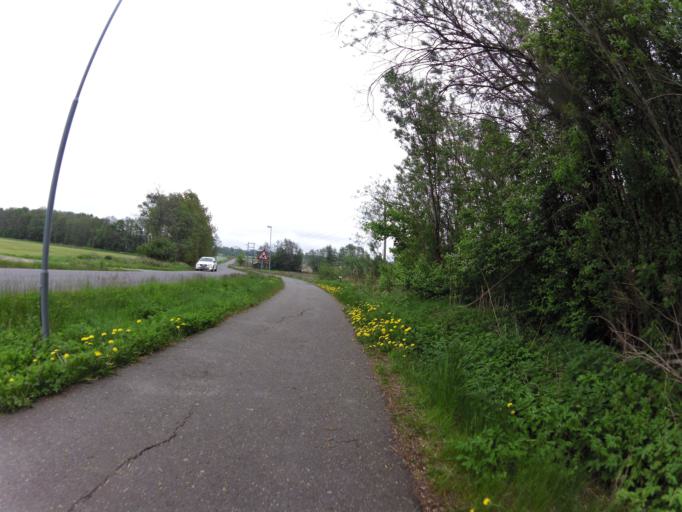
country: NO
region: Ostfold
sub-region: Moss
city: Moss
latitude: 59.3847
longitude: 10.6634
